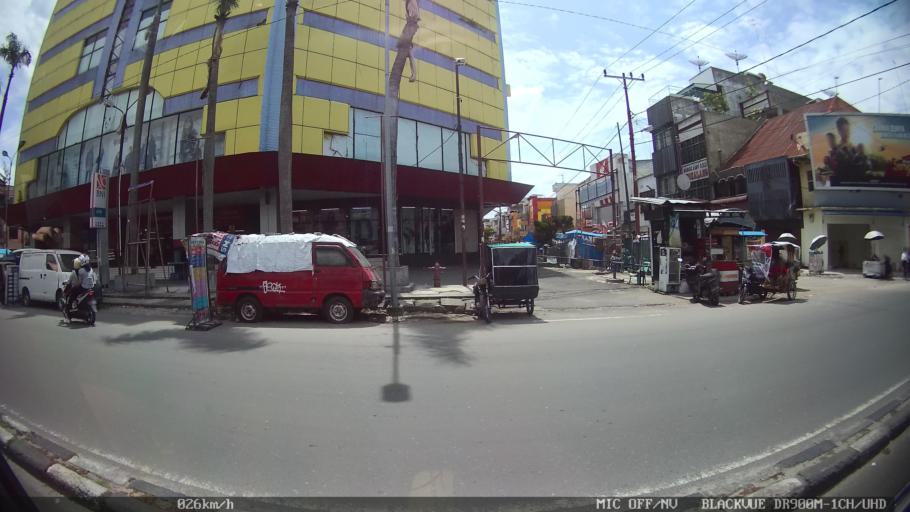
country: ID
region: North Sumatra
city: Medan
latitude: 3.5807
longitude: 98.6607
